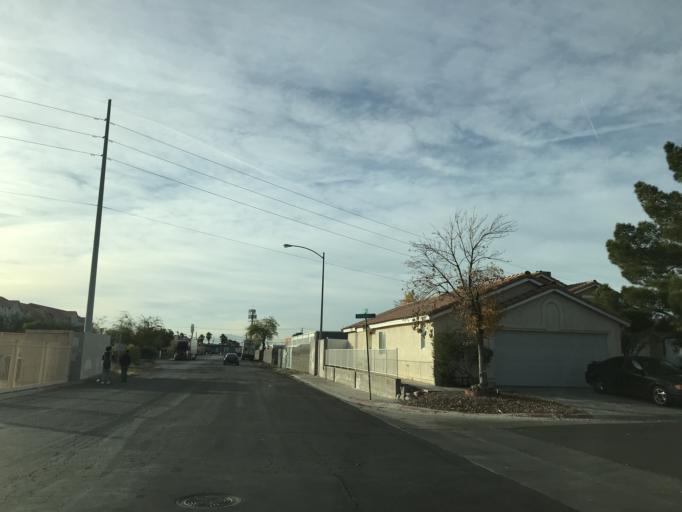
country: US
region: Nevada
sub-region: Clark County
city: Nellis Air Force Base
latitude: 36.2431
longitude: -115.0577
